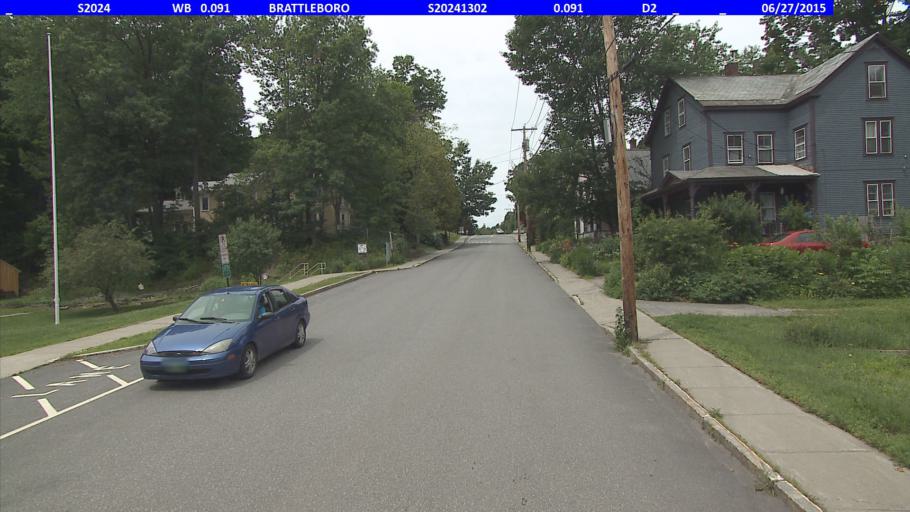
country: US
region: Vermont
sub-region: Windham County
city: Brattleboro
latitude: 42.8522
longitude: -72.5648
